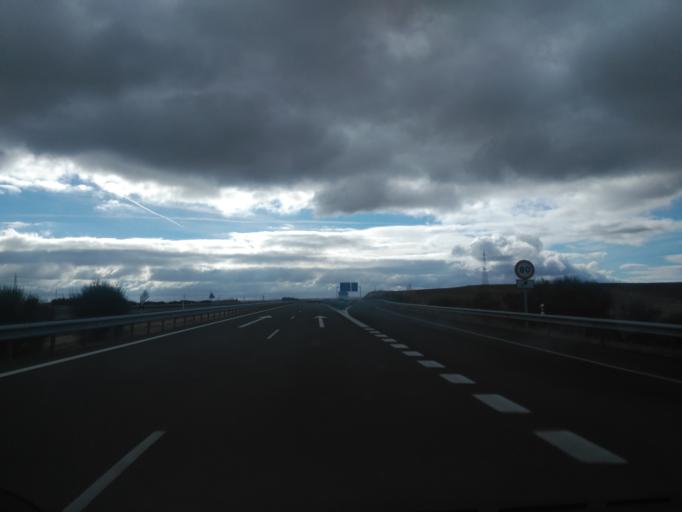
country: ES
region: Castille and Leon
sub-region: Provincia de Palencia
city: Abia de las Torres
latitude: 42.4116
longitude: -4.3887
